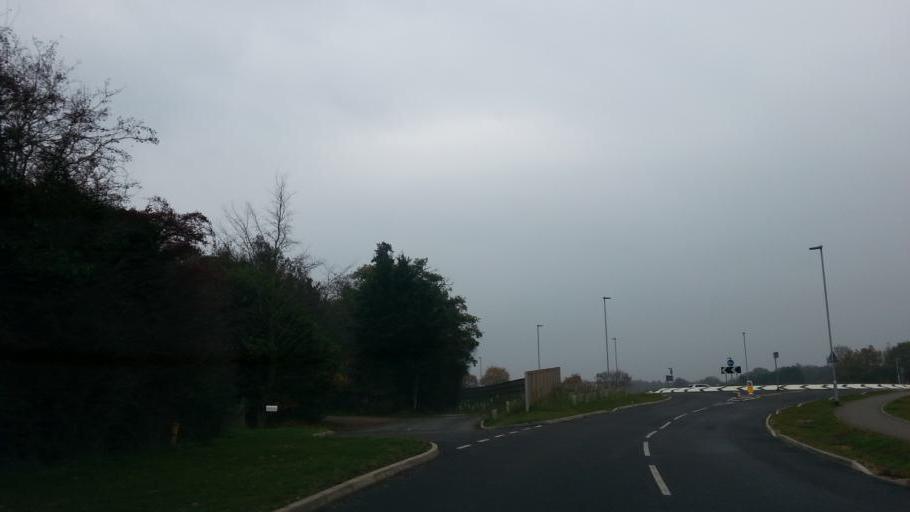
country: GB
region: England
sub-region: Suffolk
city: Thurston
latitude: 52.2462
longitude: 0.7803
